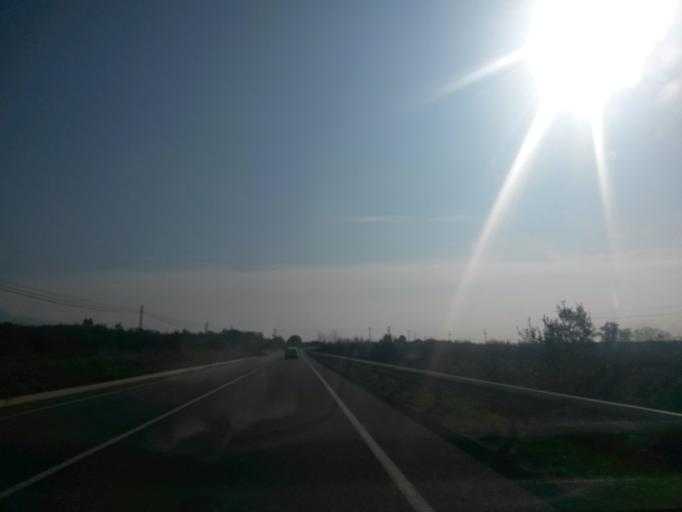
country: ES
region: Catalonia
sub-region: Provincia de Girona
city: Vilajuiga
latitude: 42.3299
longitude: 3.0866
